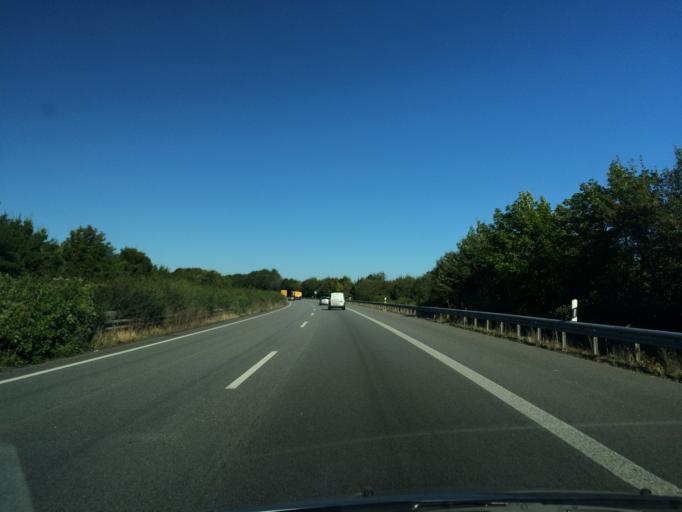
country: DE
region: Rheinland-Pfalz
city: Contwig
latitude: 49.2273
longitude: 7.4340
